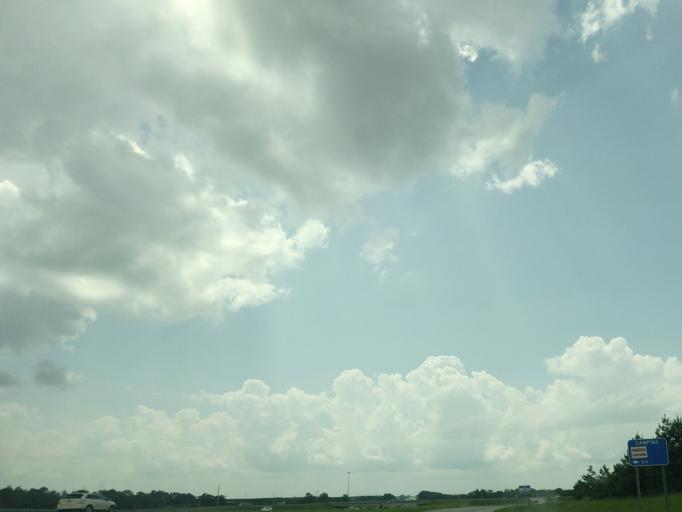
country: US
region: Georgia
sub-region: Houston County
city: Perry
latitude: 32.5502
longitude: -83.7444
